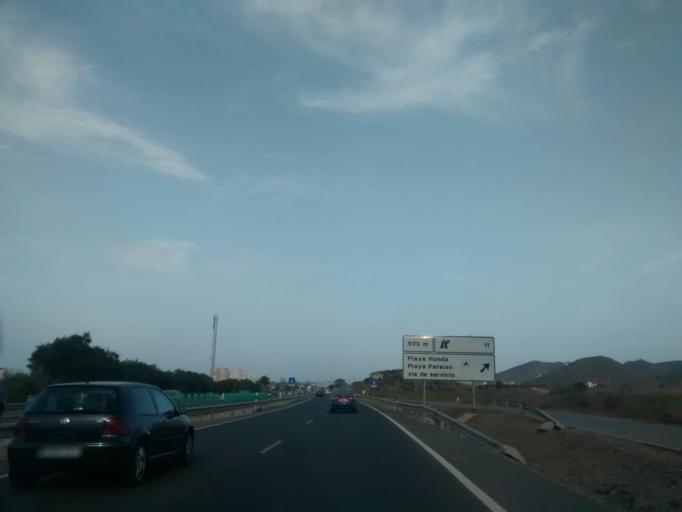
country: ES
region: Murcia
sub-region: Murcia
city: La Manga del Mar Menor
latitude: 37.6236
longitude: -0.7485
